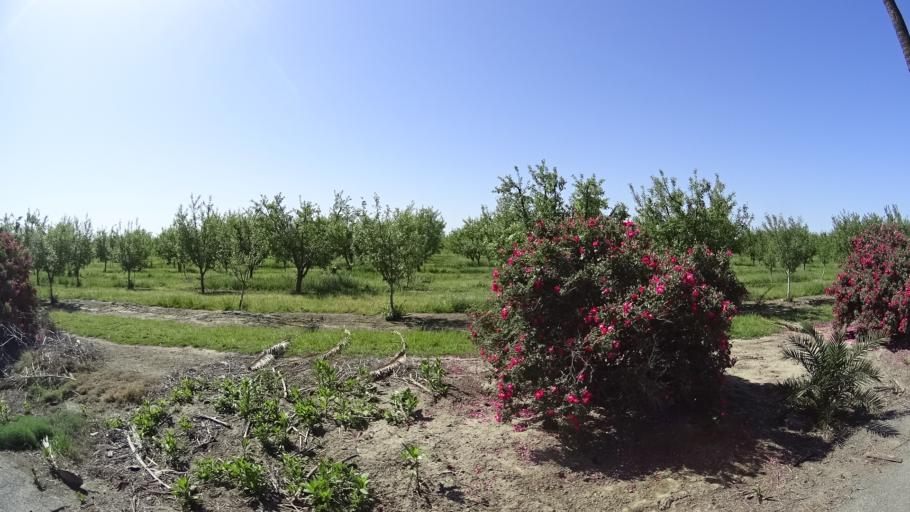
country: US
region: California
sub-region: Glenn County
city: Hamilton City
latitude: 39.7374
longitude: -122.0352
